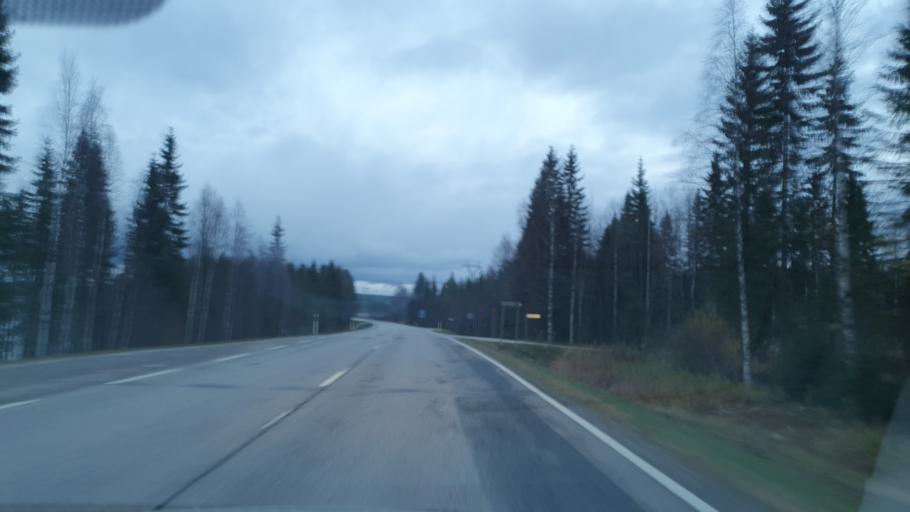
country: FI
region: Kainuu
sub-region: Kehys-Kainuu
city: Hyrynsalmi
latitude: 64.5974
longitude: 28.4493
